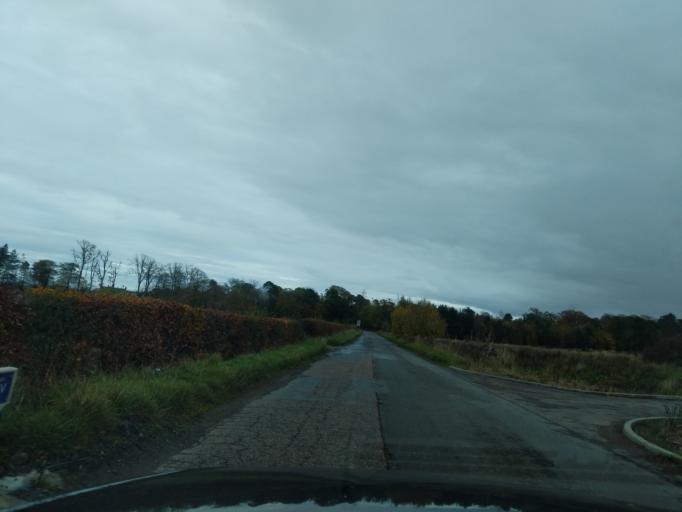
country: GB
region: Scotland
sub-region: Fife
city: Saint Andrews
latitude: 56.2880
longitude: -2.8263
